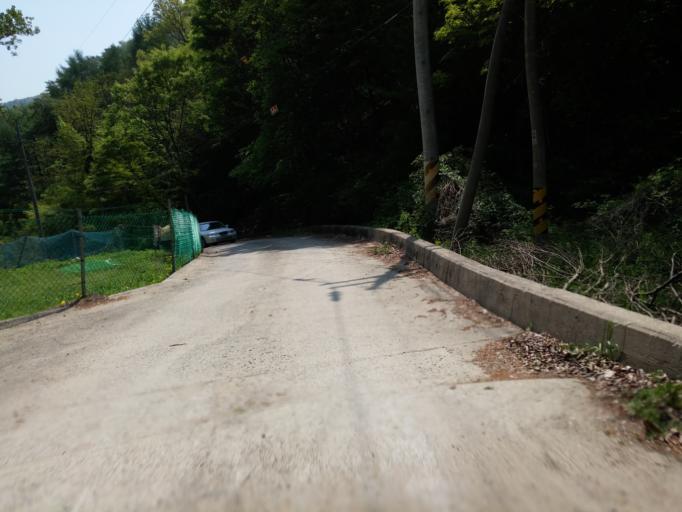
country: KR
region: Chungcheongbuk-do
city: Okcheon
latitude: 36.4130
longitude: 127.5974
